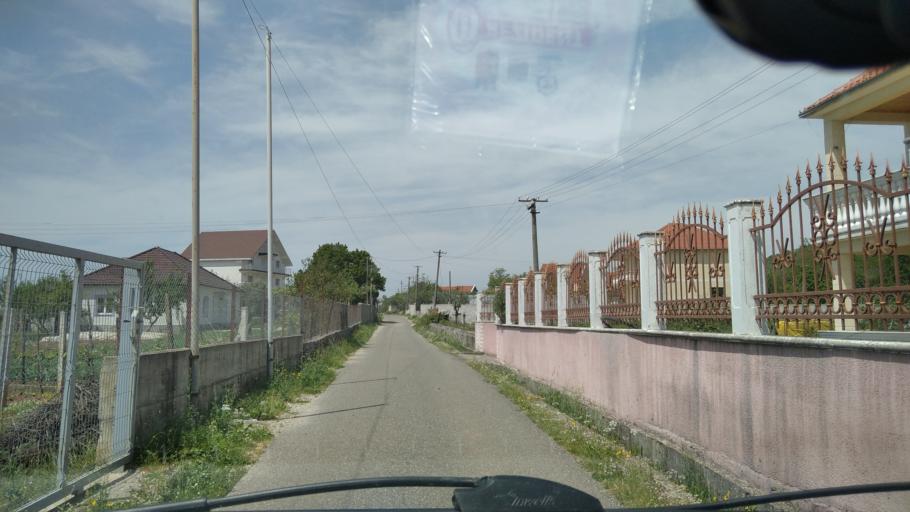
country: AL
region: Shkoder
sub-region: Rrethi i Malesia e Madhe
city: Gruemire
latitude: 42.1462
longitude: 19.5441
